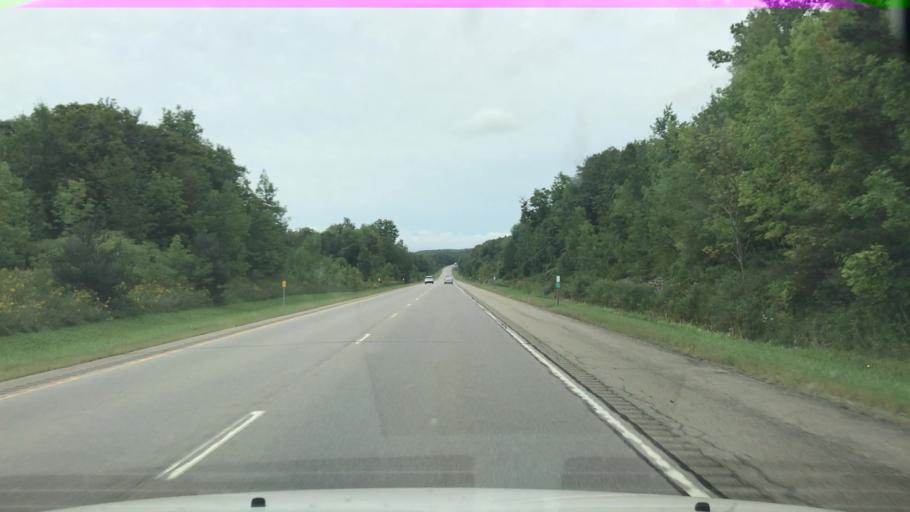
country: US
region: New York
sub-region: Erie County
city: Springville
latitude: 42.5833
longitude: -78.7295
